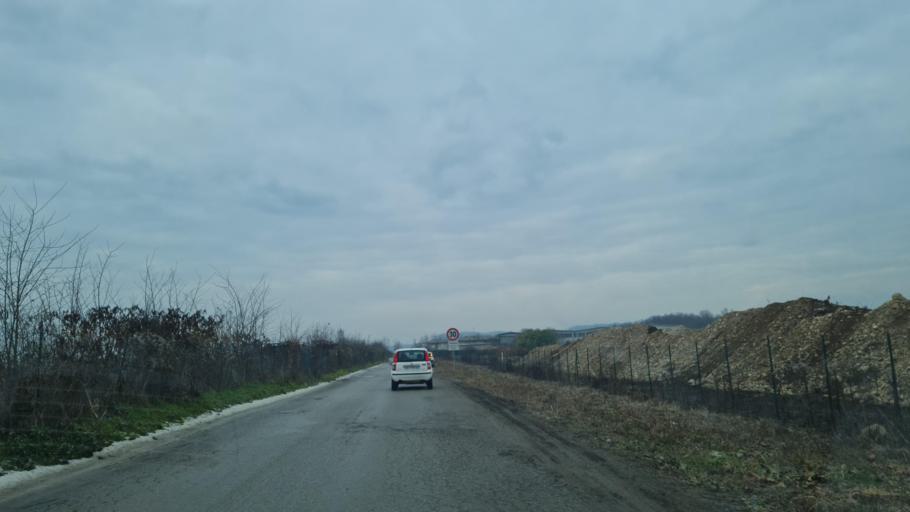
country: IT
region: Piedmont
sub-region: Provincia di Biella
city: Cavaglia
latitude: 45.3814
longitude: 8.1138
